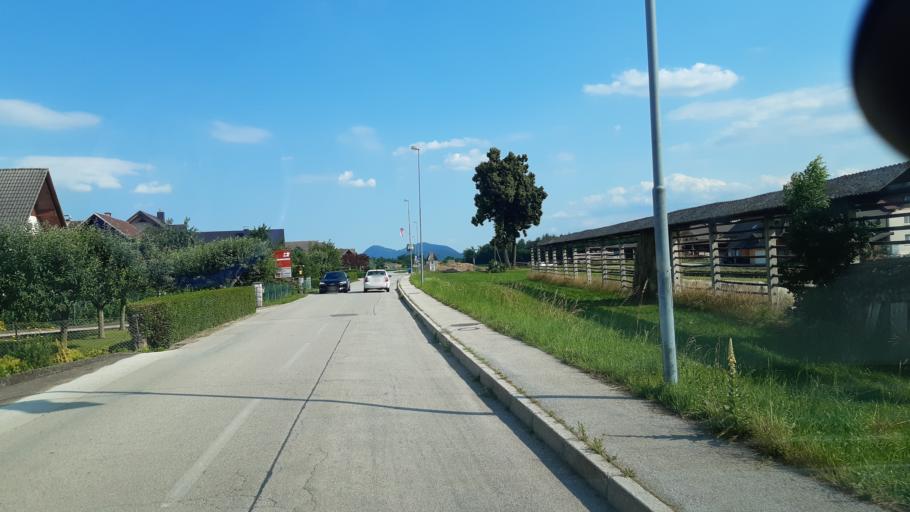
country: SI
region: Sencur
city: Hrastje
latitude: 46.2108
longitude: 14.3981
